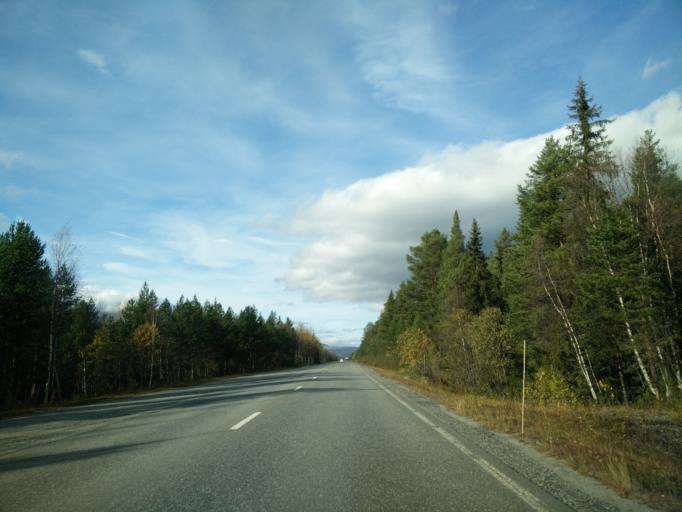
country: NO
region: Hedmark
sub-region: Engerdal
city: Engerdal
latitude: 62.5283
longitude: 12.5747
